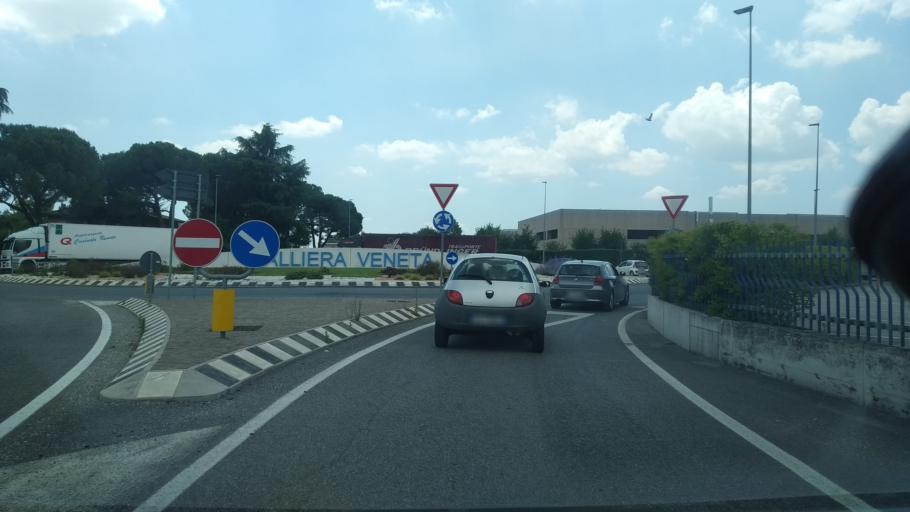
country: IT
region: Veneto
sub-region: Provincia di Padova
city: Galliera Veneta
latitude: 45.6657
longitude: 11.8186
